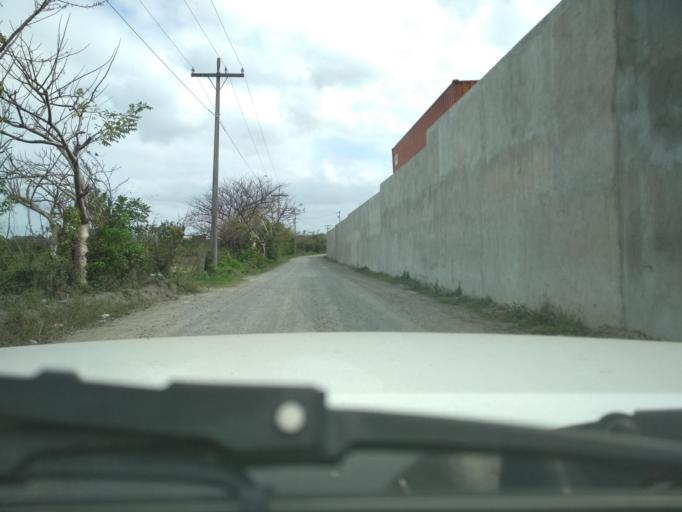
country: MX
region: Veracruz
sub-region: Veracruz
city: Delfino Victoria (Santa Fe)
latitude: 19.2435
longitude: -96.2568
